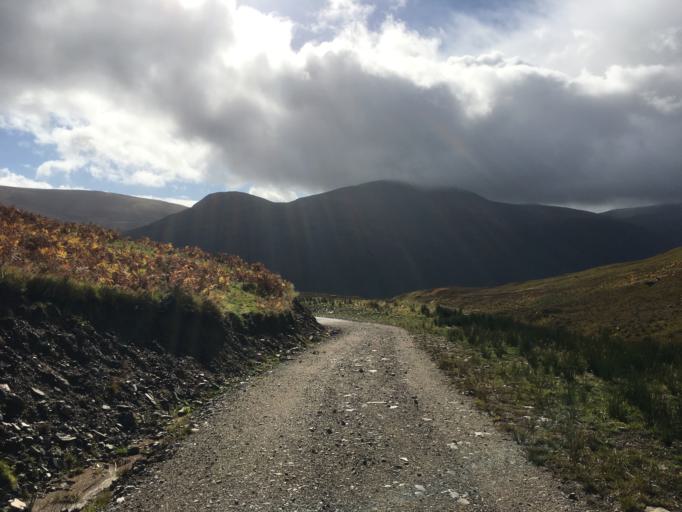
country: GB
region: Scotland
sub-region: Highland
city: Spean Bridge
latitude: 57.3488
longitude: -4.9828
